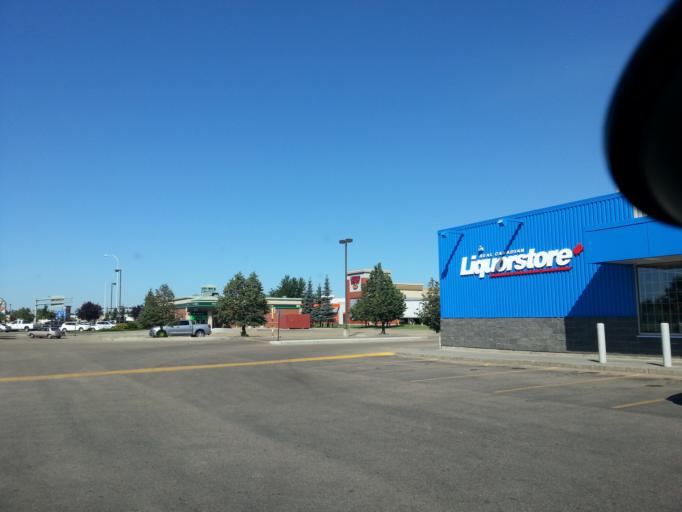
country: CA
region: Alberta
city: St. Albert
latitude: 53.6210
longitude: -113.6060
